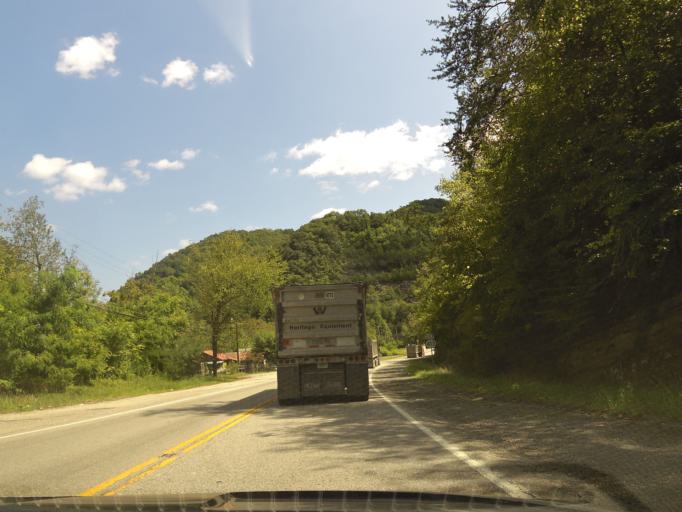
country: US
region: Kentucky
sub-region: Harlan County
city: Harlan
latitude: 36.8686
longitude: -83.3191
